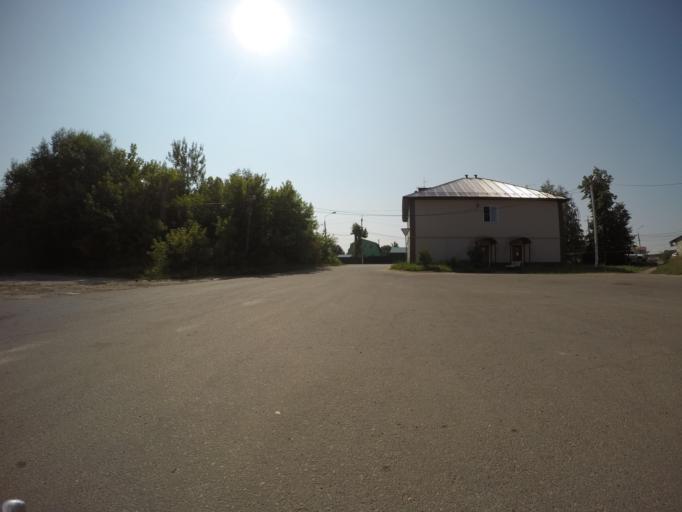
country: RU
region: Moskovskaya
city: Rechitsy
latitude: 55.6143
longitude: 38.5358
